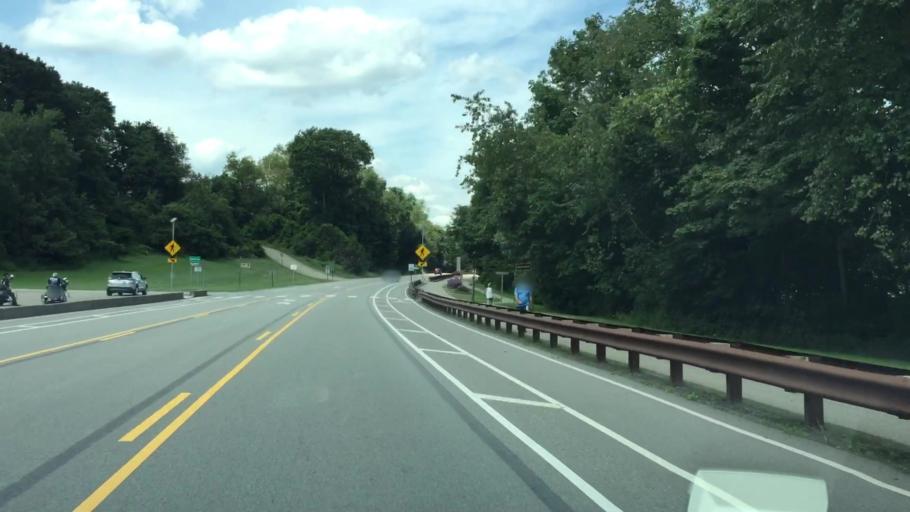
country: US
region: Pennsylvania
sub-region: Allegheny County
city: South Park Township
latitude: 40.3089
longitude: -80.0011
